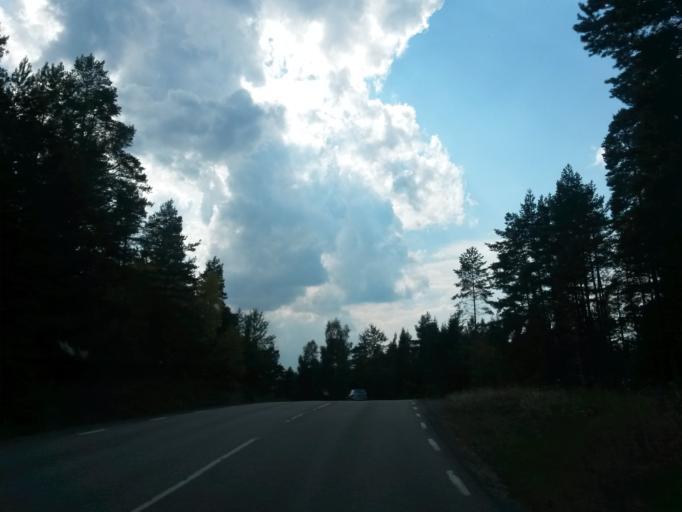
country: SE
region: Vaestra Goetaland
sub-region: Lidkopings Kommun
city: Lidkoping
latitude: 58.6231
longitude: 13.1291
